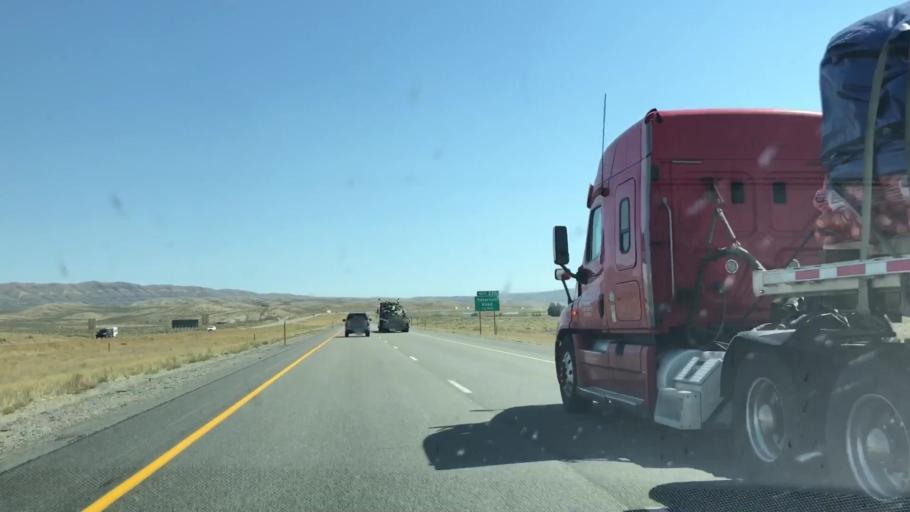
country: US
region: Wyoming
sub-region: Carbon County
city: Saratoga
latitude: 41.7420
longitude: -106.7833
